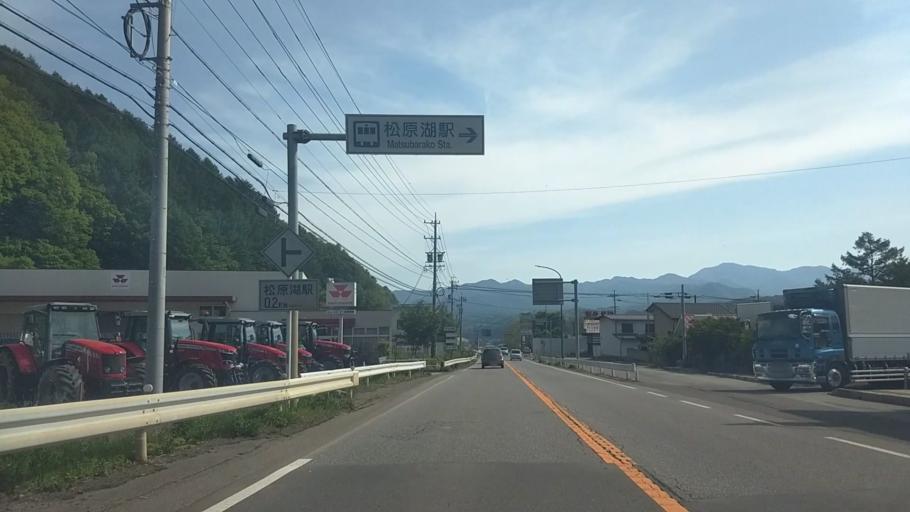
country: JP
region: Nagano
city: Saku
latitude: 36.0618
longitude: 138.4696
